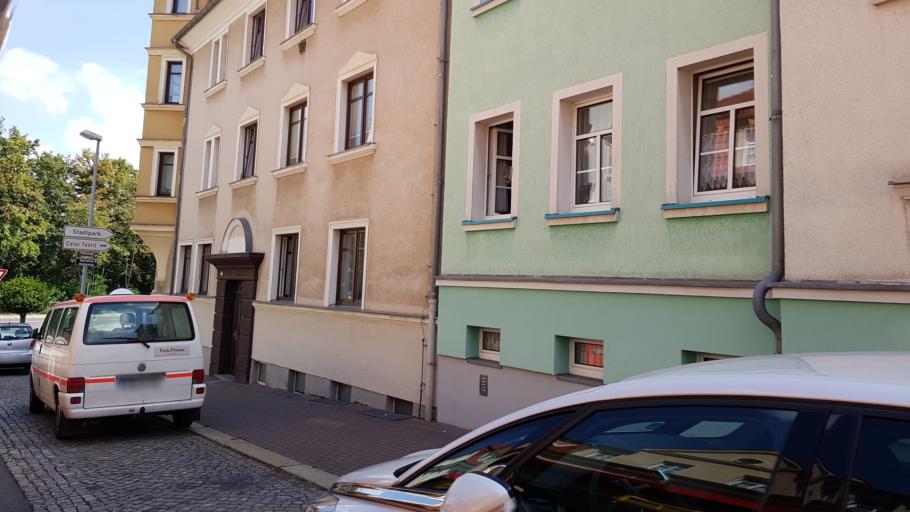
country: DE
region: Saxony
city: Frankenberg
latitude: 50.9077
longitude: 13.0358
